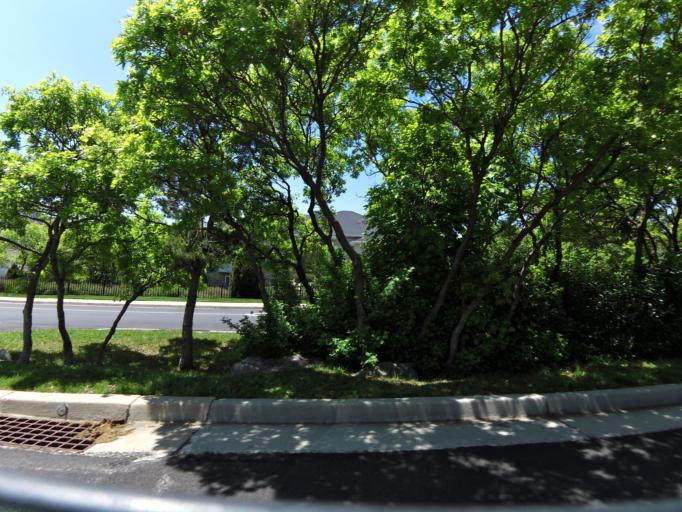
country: US
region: Utah
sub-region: Weber County
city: Uintah
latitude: 41.1695
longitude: -111.9279
